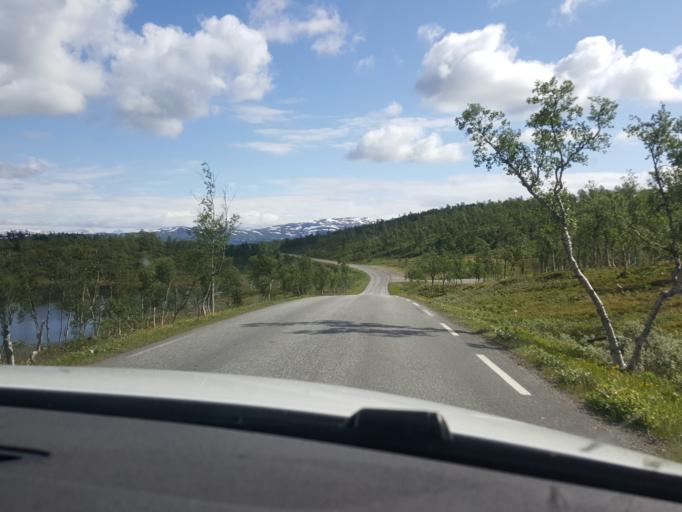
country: NO
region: Nordland
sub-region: Saltdal
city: Rognan
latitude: 67.0346
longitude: 15.1861
